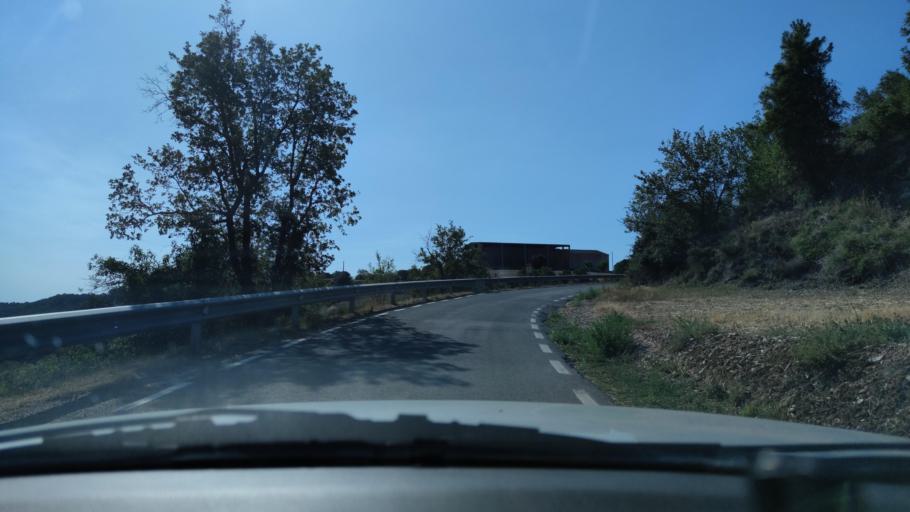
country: ES
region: Catalonia
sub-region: Provincia de Lleida
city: Ivorra
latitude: 41.7330
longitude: 1.3606
